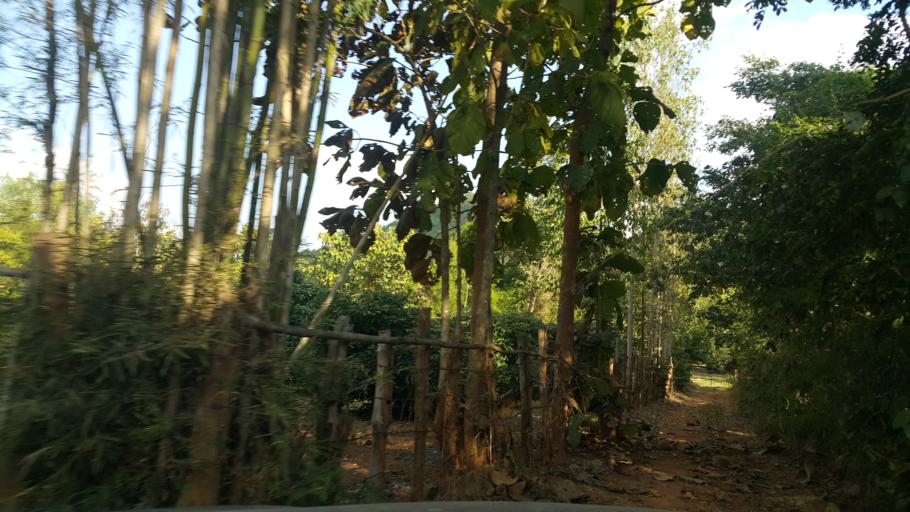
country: TH
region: Lamphun
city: Mae Tha
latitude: 18.5287
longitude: 99.1115
